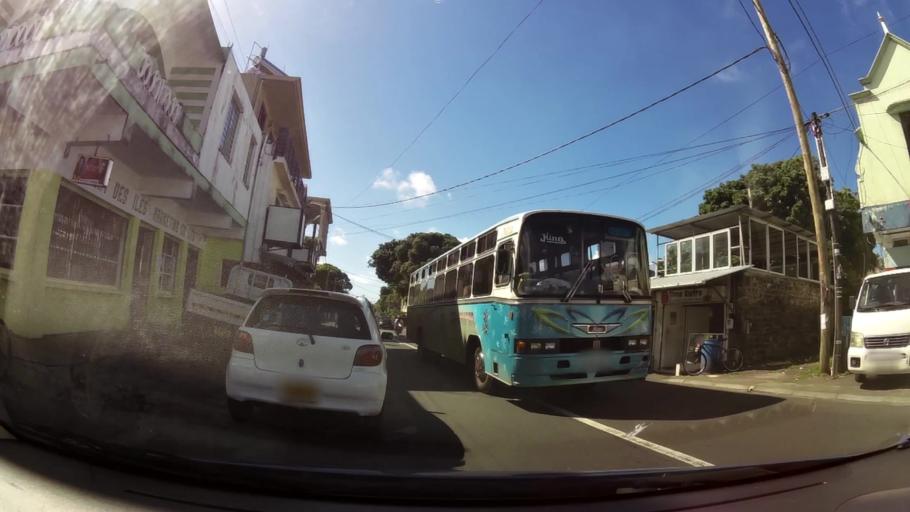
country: MU
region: Grand Port
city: Plaine Magnien
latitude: -20.4316
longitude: 57.6641
